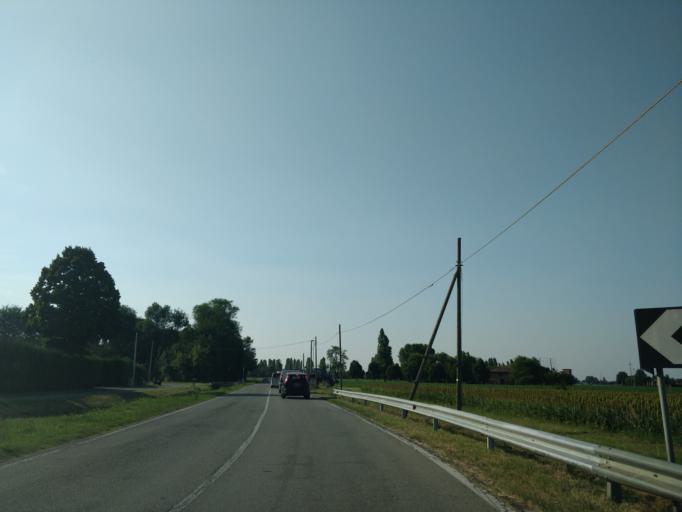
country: IT
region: Emilia-Romagna
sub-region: Provincia di Bologna
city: Argelato
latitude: 44.6188
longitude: 11.3378
